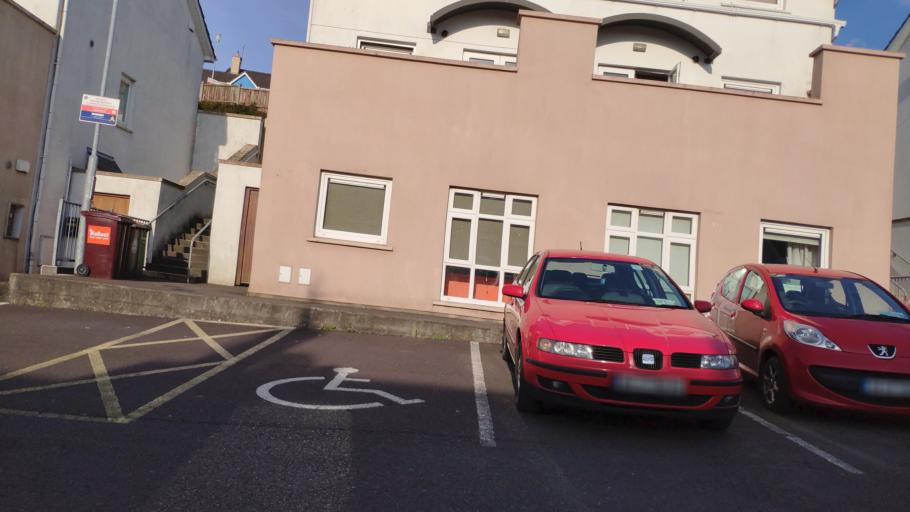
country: IE
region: Munster
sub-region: County Cork
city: Cork
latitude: 51.9086
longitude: -8.4709
